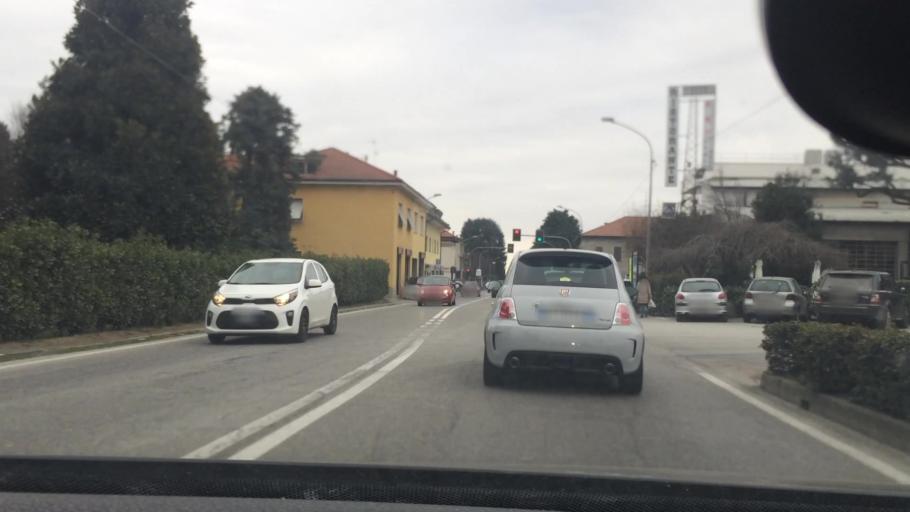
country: IT
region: Lombardy
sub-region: Provincia di Monza e Brianza
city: Lentate sul Seveso
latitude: 45.6776
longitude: 9.1152
